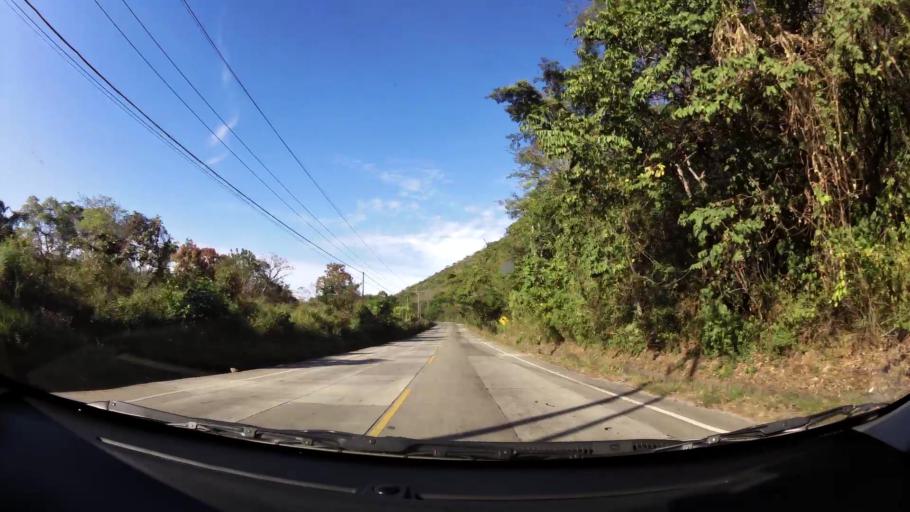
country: SV
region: Santa Ana
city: Metapan
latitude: 14.2608
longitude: -89.4601
